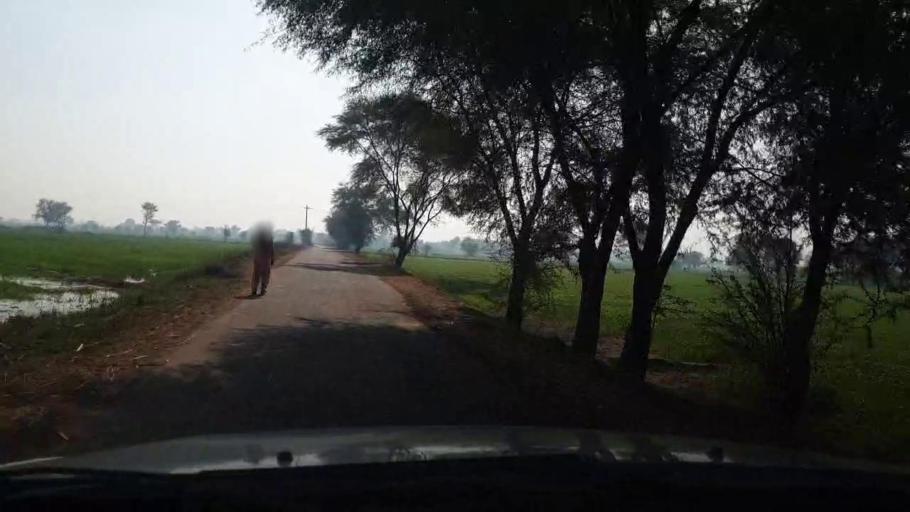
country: PK
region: Sindh
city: Khanpur
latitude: 27.7426
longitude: 69.5047
